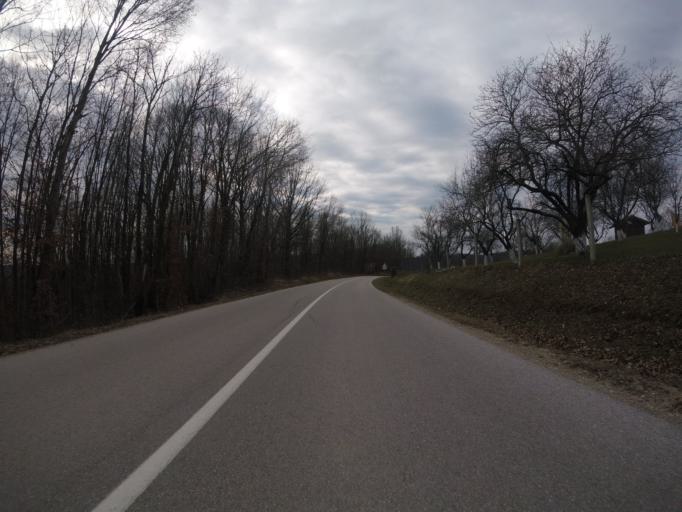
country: HR
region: Zagrebacka
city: Mraclin
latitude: 45.5398
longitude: 16.0598
